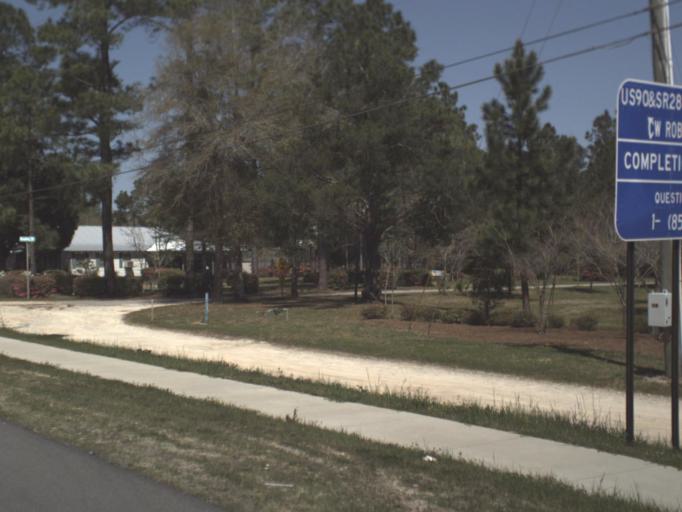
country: US
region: Florida
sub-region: Walton County
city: DeFuniak Springs
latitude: 30.7314
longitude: -86.1404
